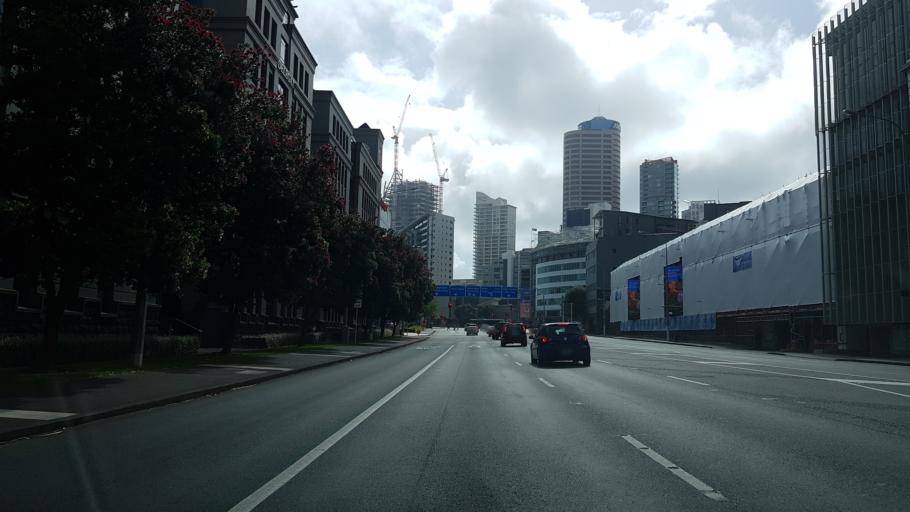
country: NZ
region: Auckland
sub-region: Auckland
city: Auckland
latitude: -36.8458
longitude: 174.7588
